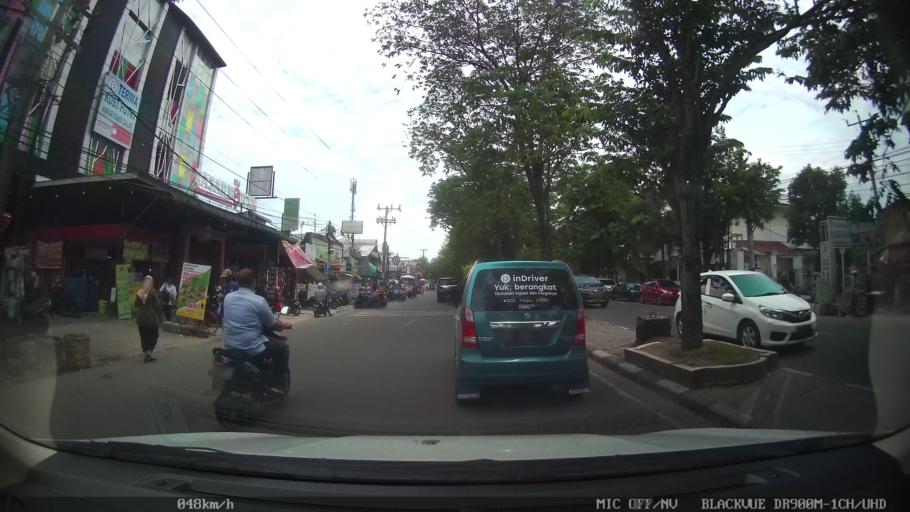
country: ID
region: North Sumatra
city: Medan
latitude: 3.5597
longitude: 98.6617
